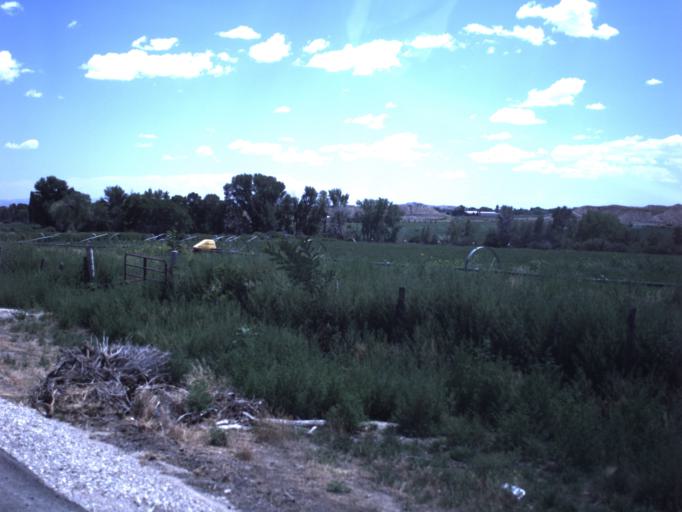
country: US
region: Utah
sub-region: Emery County
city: Orangeville
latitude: 39.2470
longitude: -111.0729
